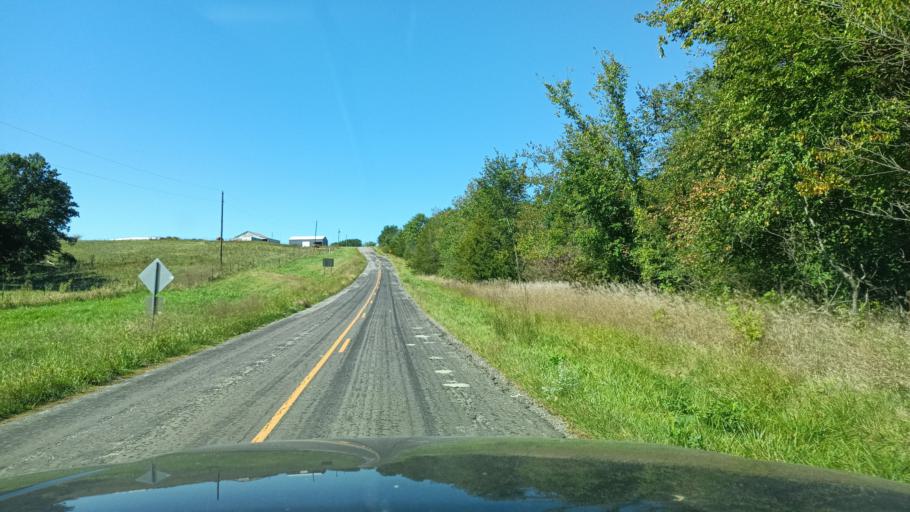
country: US
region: Missouri
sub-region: Scotland County
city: Memphis
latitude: 40.3485
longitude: -92.3261
